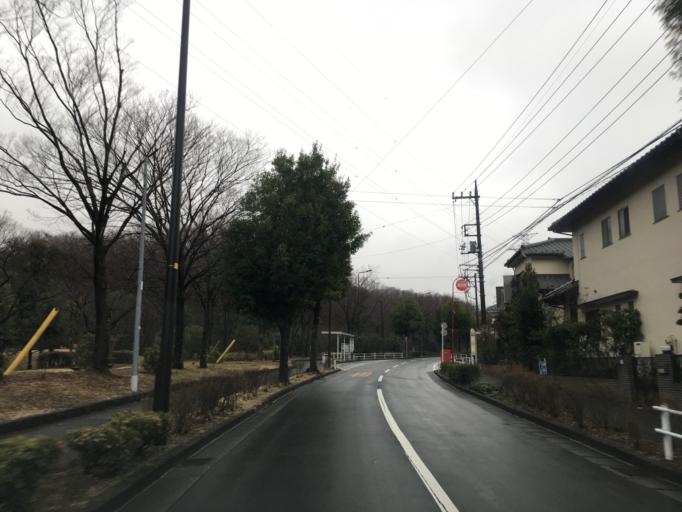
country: JP
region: Tokyo
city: Kokubunji
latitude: 35.6361
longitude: 139.4583
